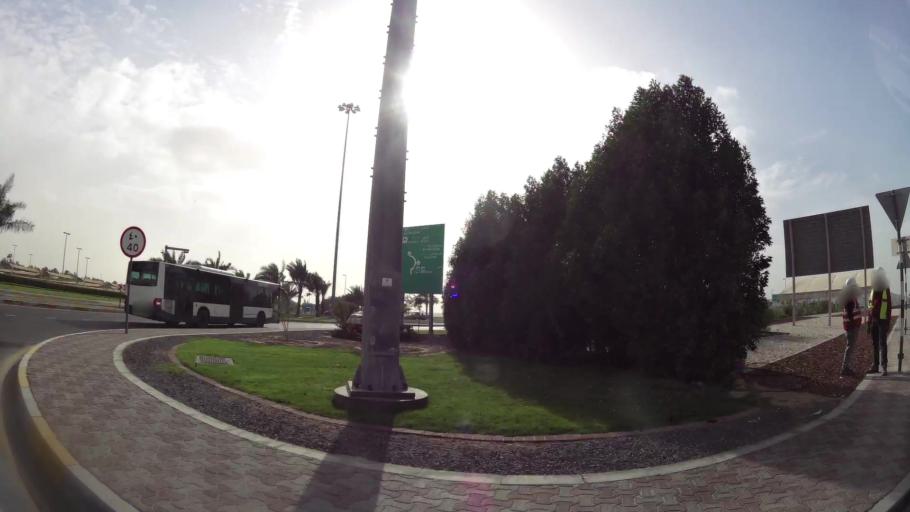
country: AE
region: Abu Dhabi
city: Abu Dhabi
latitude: 24.4266
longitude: 54.6431
